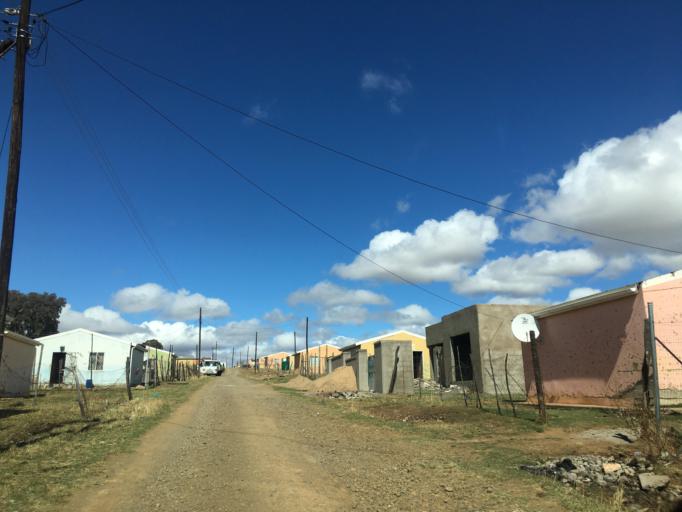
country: ZA
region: Eastern Cape
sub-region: Chris Hani District Municipality
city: Cala
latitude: -31.5409
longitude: 27.6833
